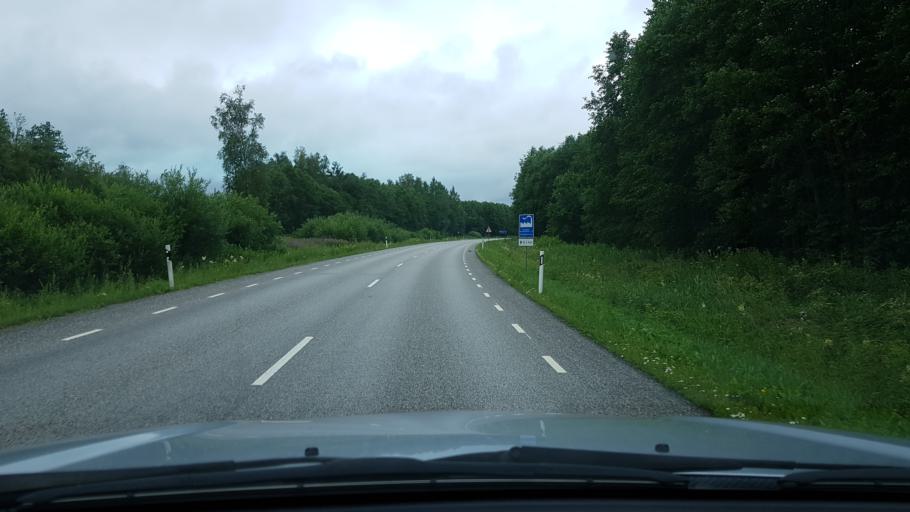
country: EE
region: Ida-Virumaa
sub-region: Narva-Joesuu linn
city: Narva-Joesuu
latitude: 59.3467
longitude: 27.9328
